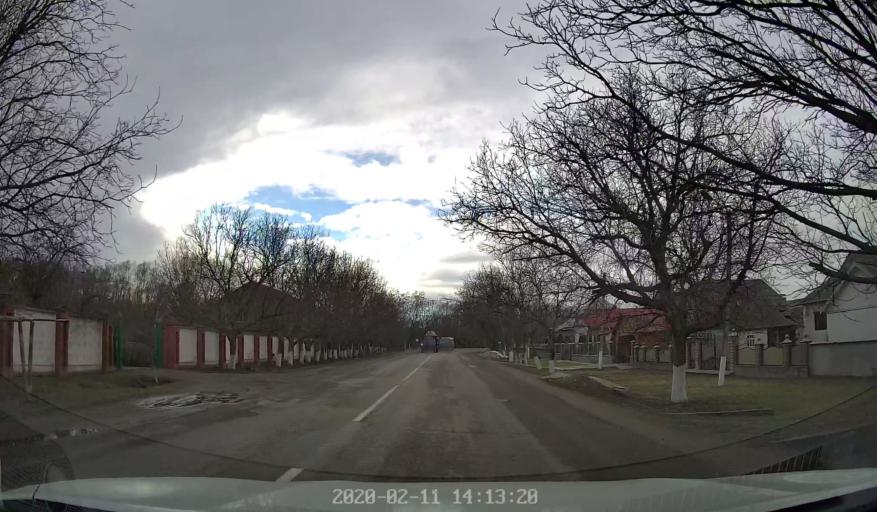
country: RO
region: Botosani
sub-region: Comuna Hudesti
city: Alba
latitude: 48.2207
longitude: 26.4746
